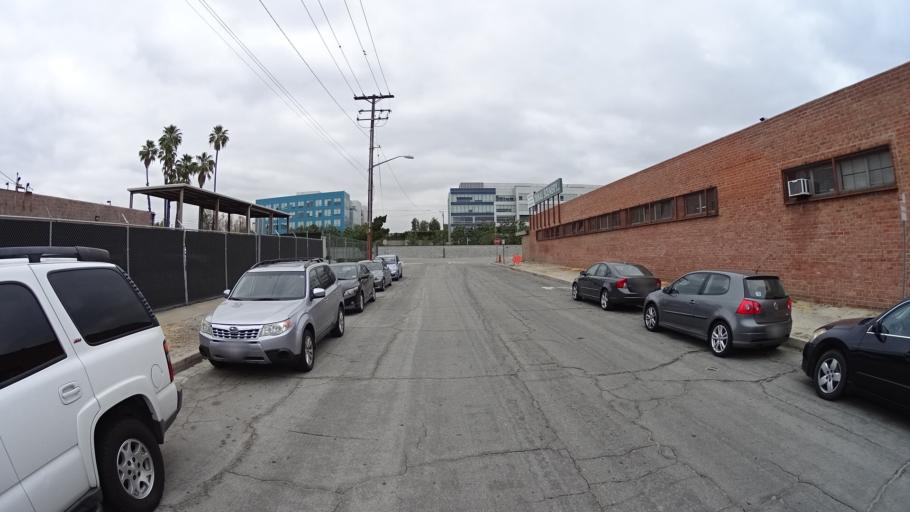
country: US
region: California
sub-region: Los Angeles County
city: North Hollywood
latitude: 34.1906
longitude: -118.3468
